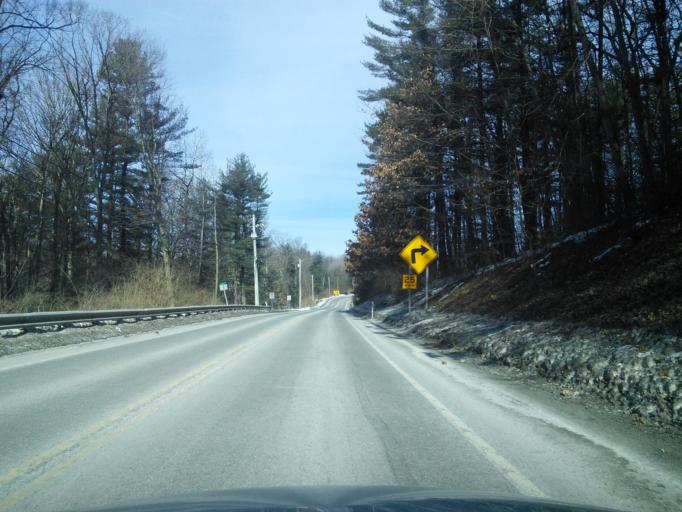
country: US
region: Pennsylvania
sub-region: Centre County
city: State College
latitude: 40.8309
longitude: -77.8802
